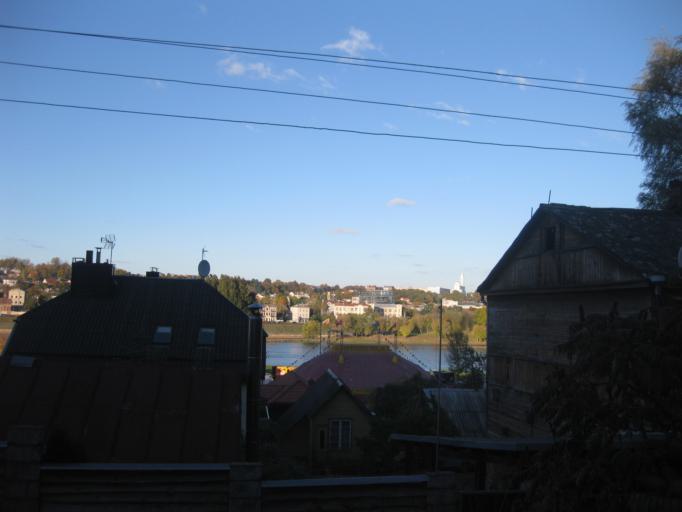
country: LT
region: Kauno apskritis
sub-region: Kaunas
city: Aleksotas
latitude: 54.8903
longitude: 23.8968
